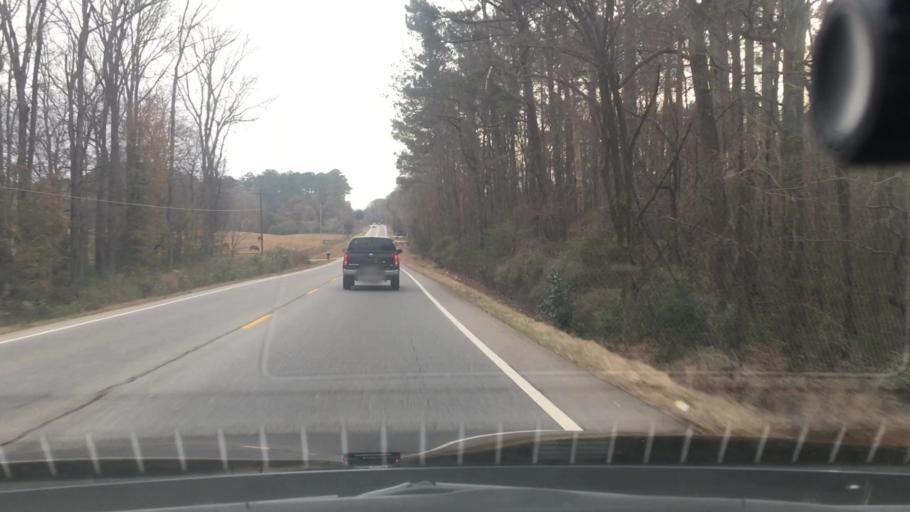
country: US
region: Georgia
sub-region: Spalding County
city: Experiment
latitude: 33.2402
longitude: -84.3371
